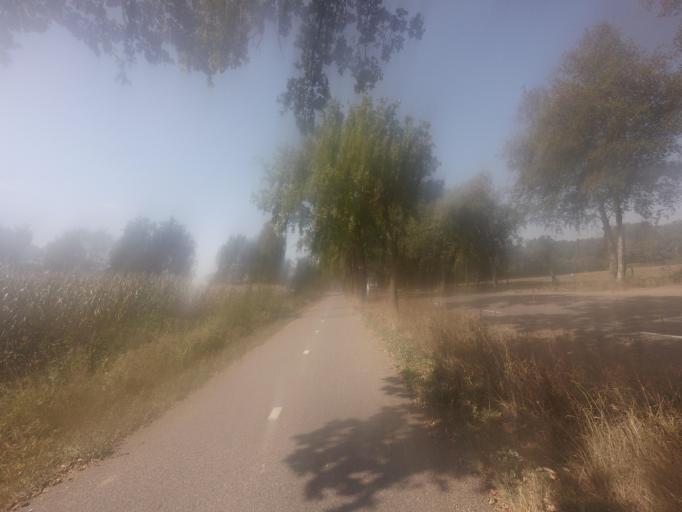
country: NL
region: North Brabant
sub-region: Gemeente Hilvarenbeek
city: Hilvarenbeek
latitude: 51.5073
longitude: 5.1056
